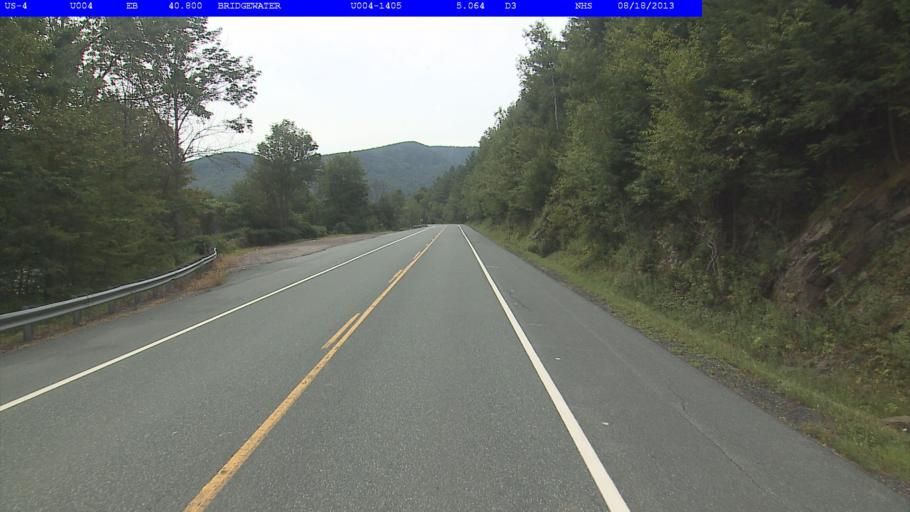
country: US
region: Vermont
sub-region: Windsor County
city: Woodstock
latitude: 43.5931
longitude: -72.6654
